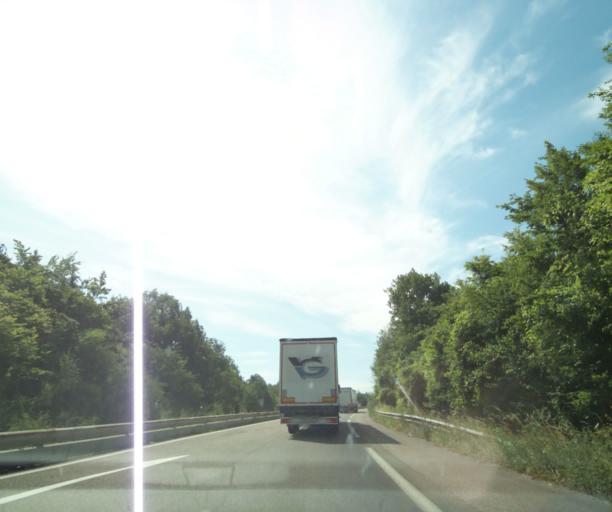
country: FR
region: Lorraine
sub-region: Departement de Meurthe-et-Moselle
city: Laxou
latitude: 48.6926
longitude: 6.1151
